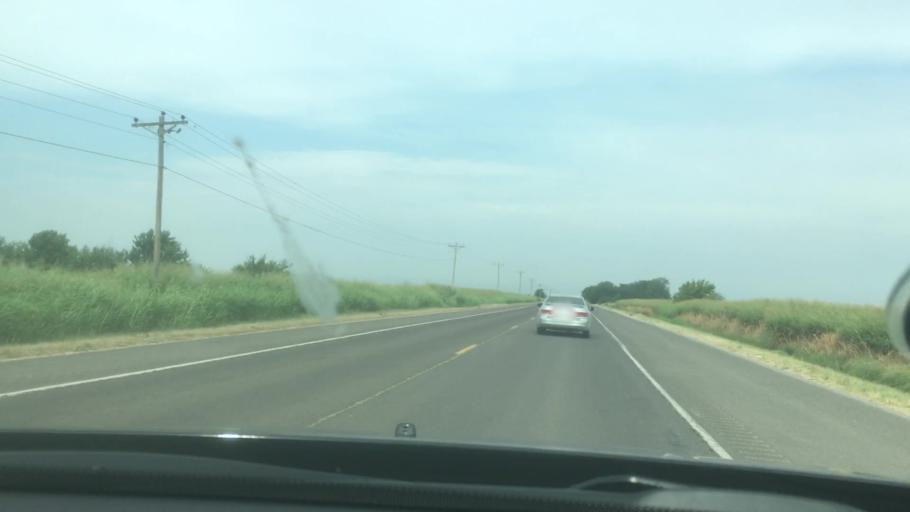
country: US
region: Oklahoma
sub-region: Garvin County
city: Maysville
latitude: 34.8192
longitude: -97.4596
